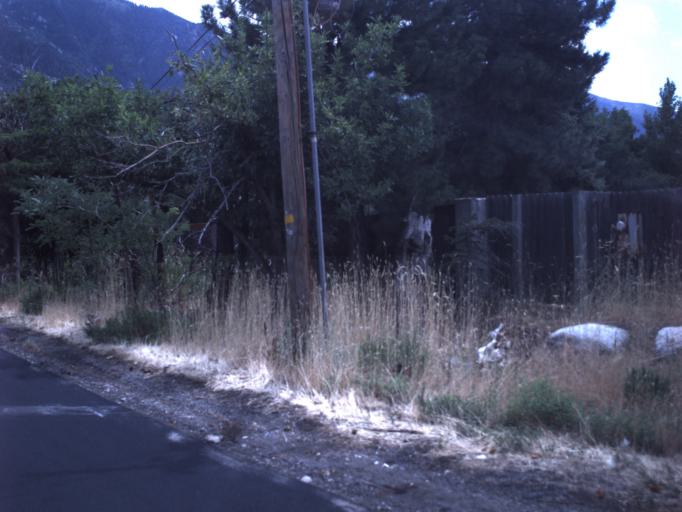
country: US
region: Utah
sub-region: Salt Lake County
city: Granite
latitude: 40.5777
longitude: -111.8025
